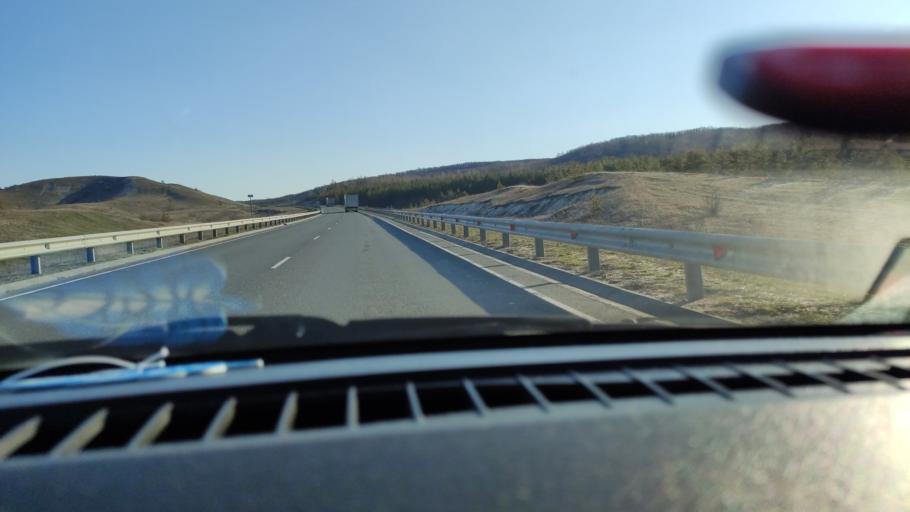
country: RU
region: Saratov
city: Alekseyevka
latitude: 52.3673
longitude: 47.9642
